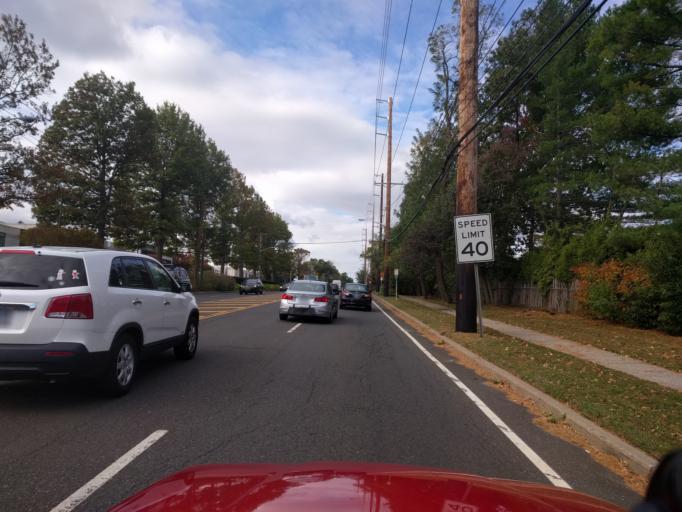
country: US
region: New York
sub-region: Nassau County
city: Munsey Park
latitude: 40.7967
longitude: -73.6713
